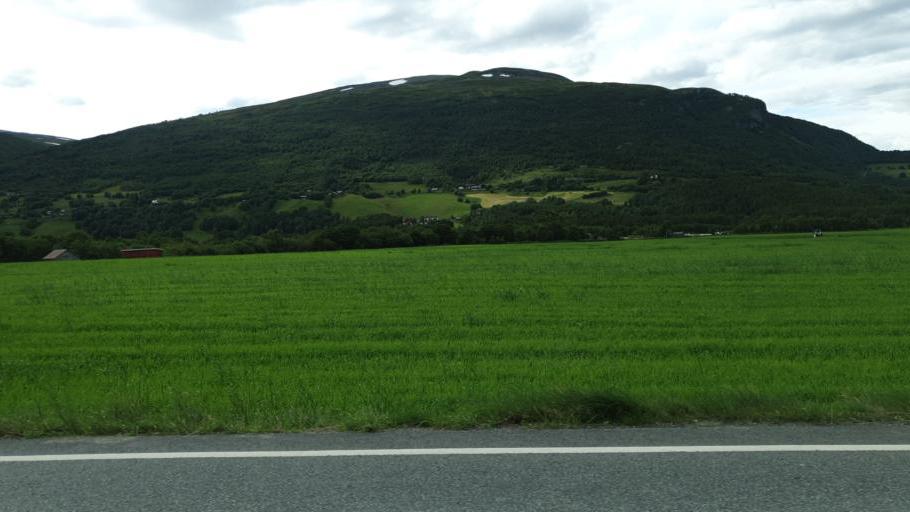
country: NO
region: Sor-Trondelag
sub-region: Oppdal
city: Oppdal
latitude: 62.5365
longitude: 9.6252
